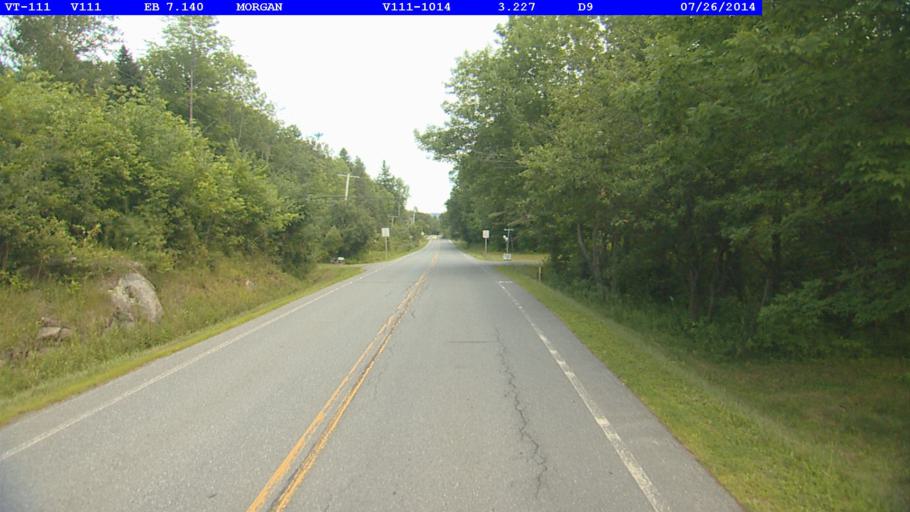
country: US
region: Vermont
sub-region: Orleans County
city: Newport
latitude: 44.9102
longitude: -72.0077
